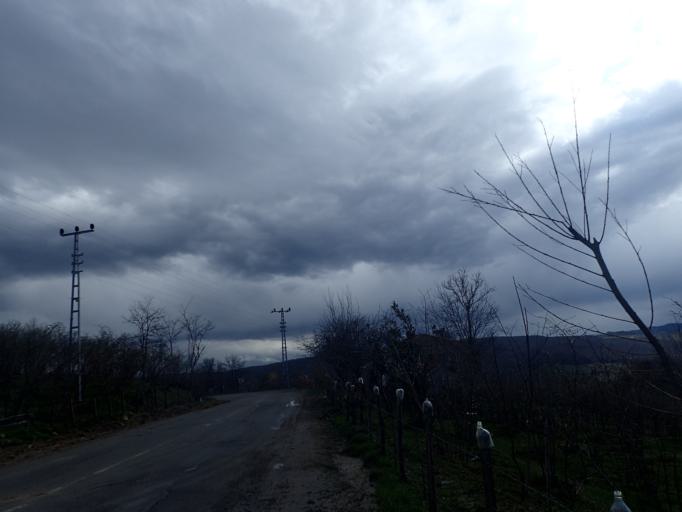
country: TR
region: Ordu
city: Kumru
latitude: 40.9311
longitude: 37.2589
